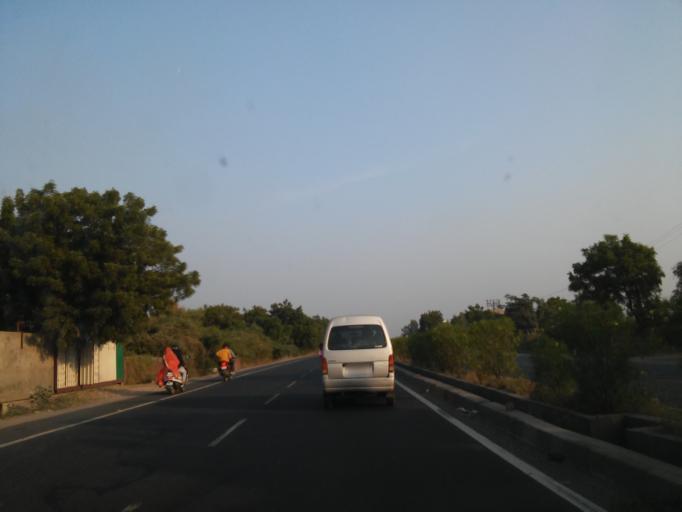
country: IN
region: Gujarat
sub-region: Ahmadabad
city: Sanand
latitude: 23.0231
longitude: 72.3208
